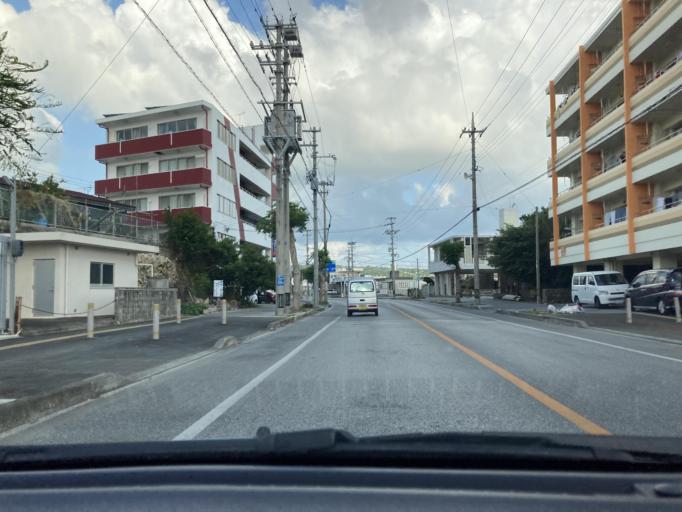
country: JP
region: Okinawa
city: Itoman
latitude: 26.1300
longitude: 127.6773
